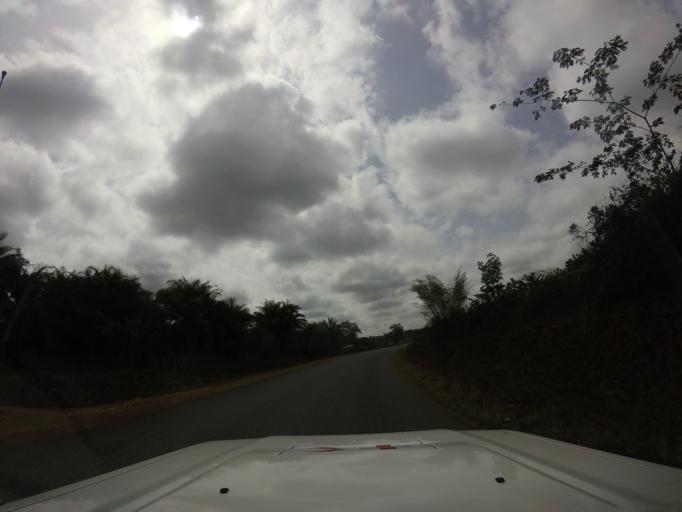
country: LR
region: Montserrado
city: Monrovia
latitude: 6.4991
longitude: -10.8126
